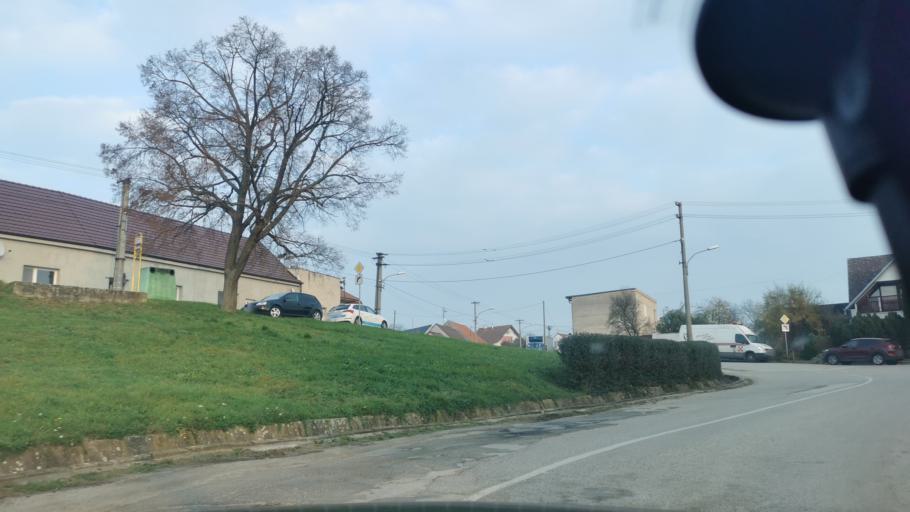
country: SK
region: Trnavsky
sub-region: Okres Skalica
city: Skalica
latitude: 48.7864
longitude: 17.2209
